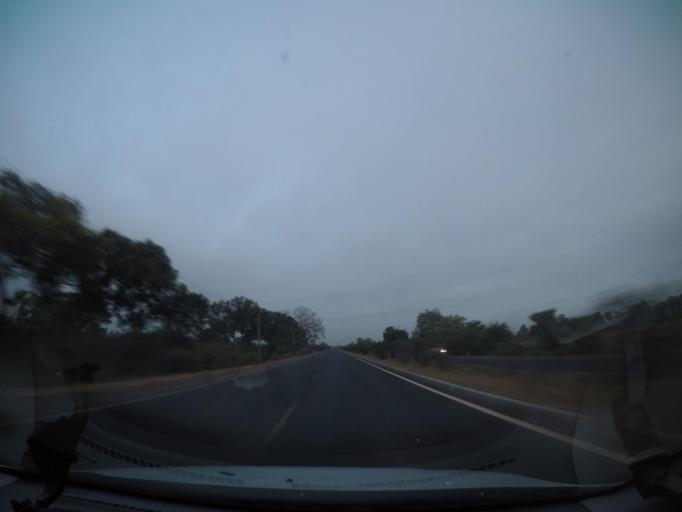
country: IN
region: Andhra Pradesh
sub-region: West Godavari
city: Tadepallegudem
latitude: 16.8101
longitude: 81.3380
